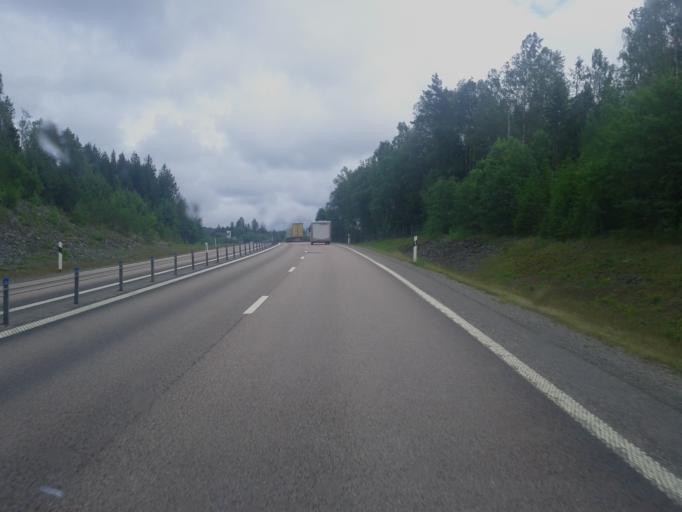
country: SE
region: Vaesternorrland
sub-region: Timra Kommun
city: Soraker
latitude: 62.5594
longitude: 17.6934
